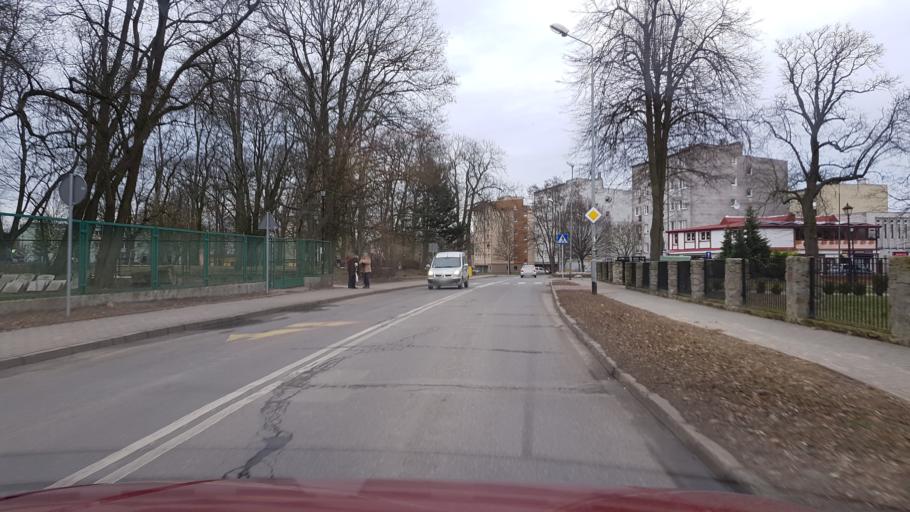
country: PL
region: West Pomeranian Voivodeship
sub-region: Powiat policki
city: Police
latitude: 53.5469
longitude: 14.5727
